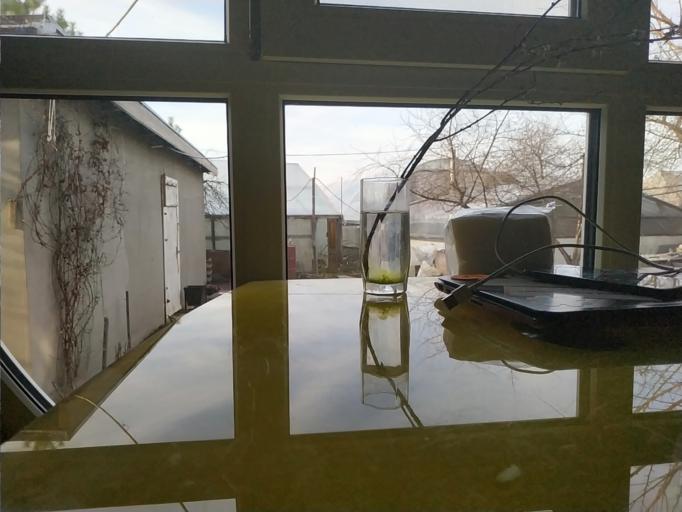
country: RU
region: Republic of Karelia
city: Suoyarvi
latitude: 61.8020
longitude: 32.3002
